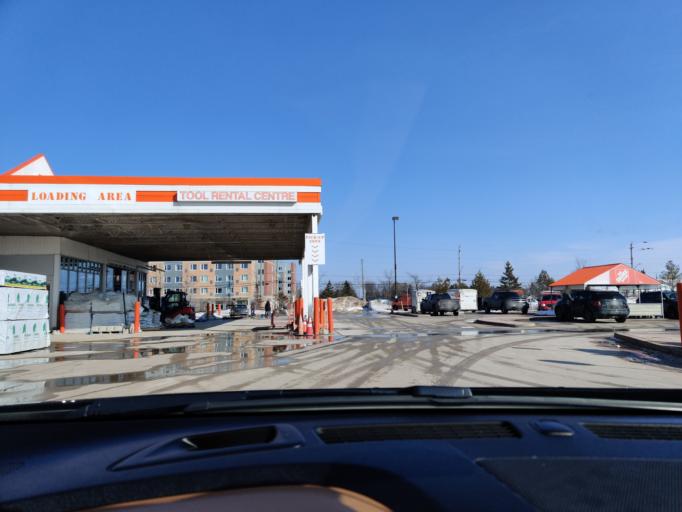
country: CA
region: Ontario
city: Collingwood
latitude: 44.4989
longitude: -80.2352
